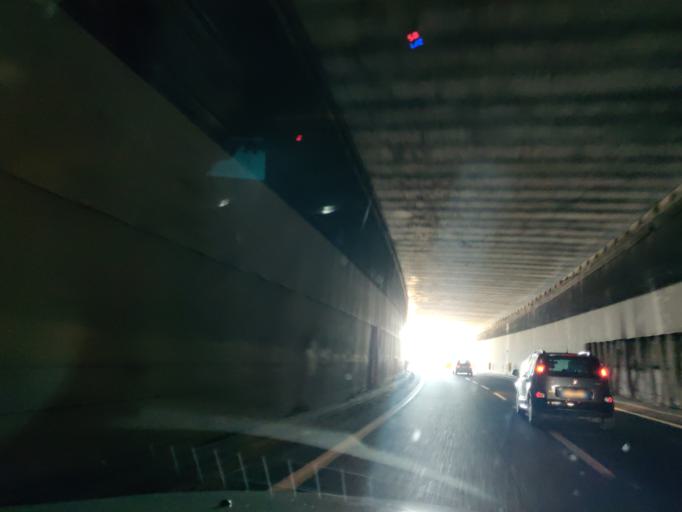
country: IT
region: Latium
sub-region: Citta metropolitana di Roma Capitale
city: Colle Verde
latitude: 41.9755
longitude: 12.5396
